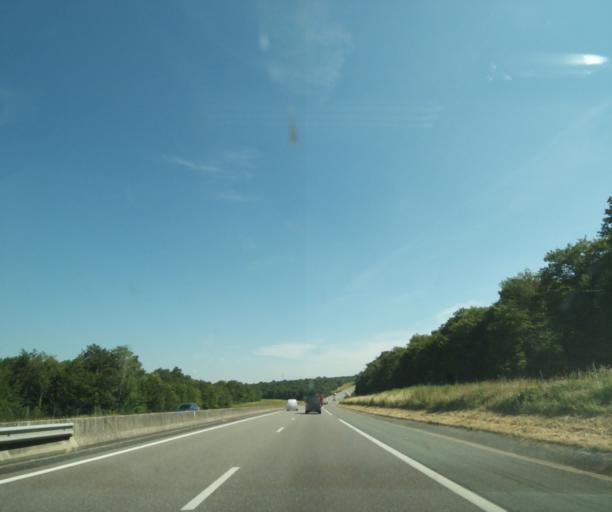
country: FR
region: Lorraine
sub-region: Departement de Meurthe-et-Moselle
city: Colombey-les-Belles
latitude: 48.4564
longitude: 5.8688
